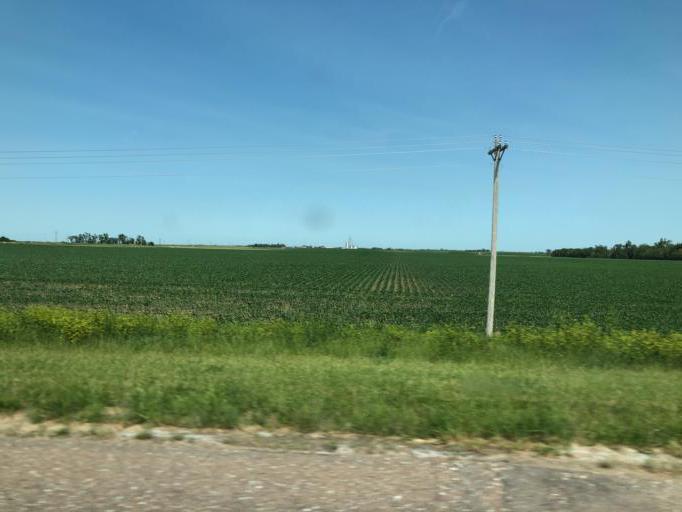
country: US
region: Nebraska
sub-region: Fillmore County
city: Geneva
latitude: 40.4194
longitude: -97.5961
